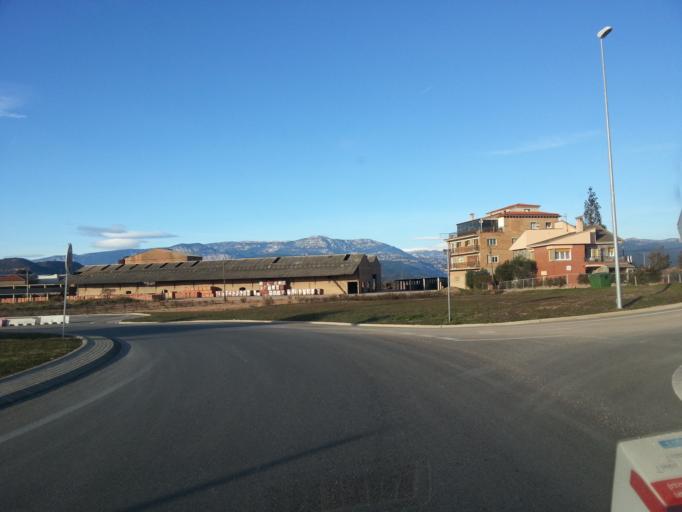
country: ES
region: Catalonia
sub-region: Provincia de Lleida
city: Olius
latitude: 41.9860
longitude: 1.5510
